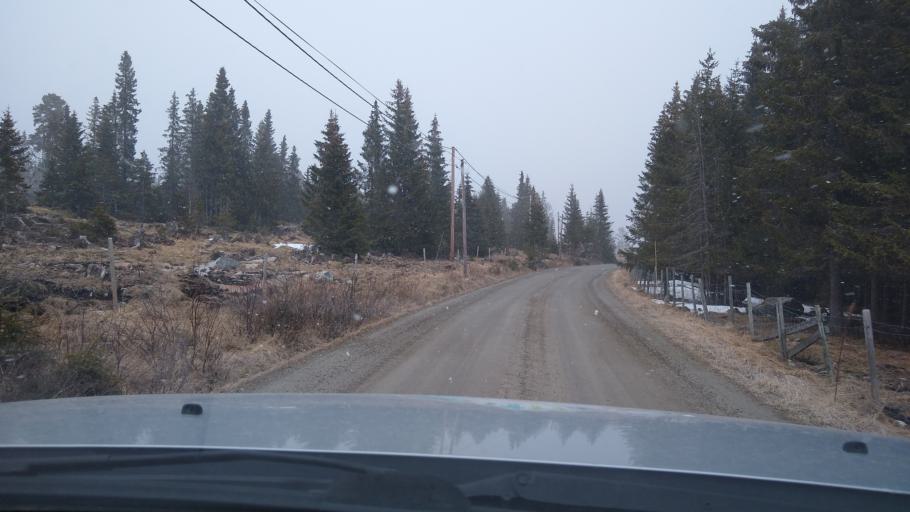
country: NO
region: Oppland
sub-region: Oyer
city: Tretten
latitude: 61.4616
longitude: 10.3411
